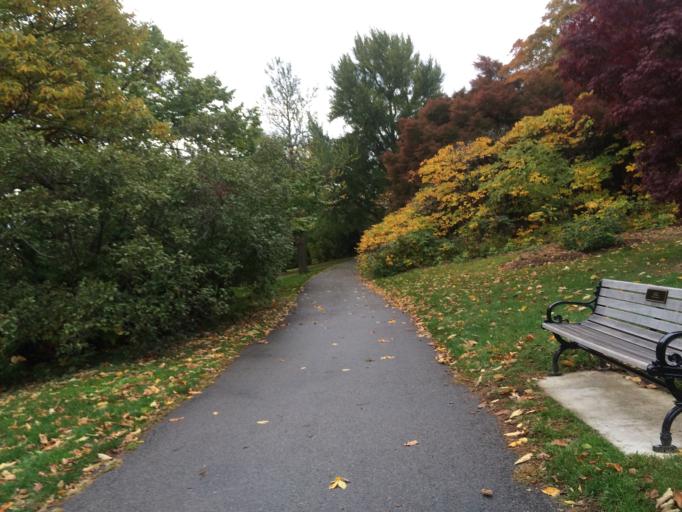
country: US
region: New York
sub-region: Monroe County
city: Rochester
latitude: 43.1303
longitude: -77.6041
